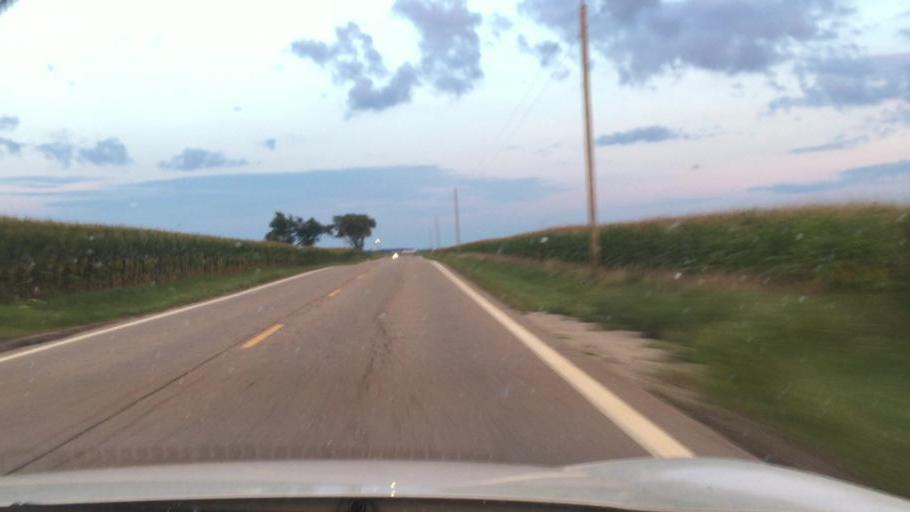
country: US
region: Ohio
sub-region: Madison County
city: Choctaw Lake
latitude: 40.0194
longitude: -83.4688
